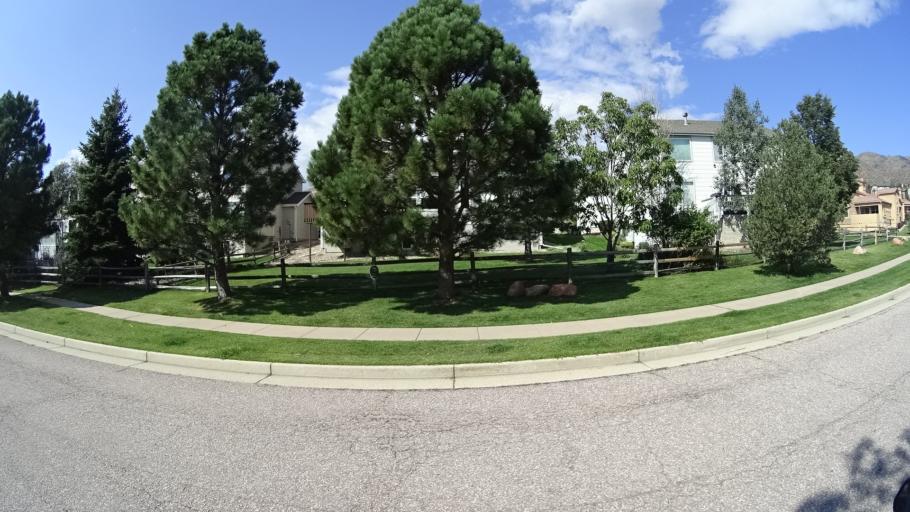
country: US
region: Colorado
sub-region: El Paso County
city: Manitou Springs
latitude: 38.9158
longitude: -104.8734
